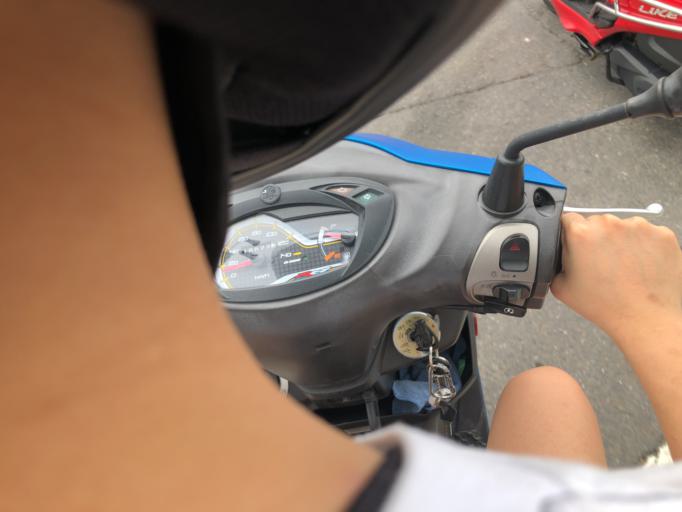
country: TW
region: Taiwan
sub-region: Taichung City
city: Taichung
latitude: 24.0899
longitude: 120.6536
